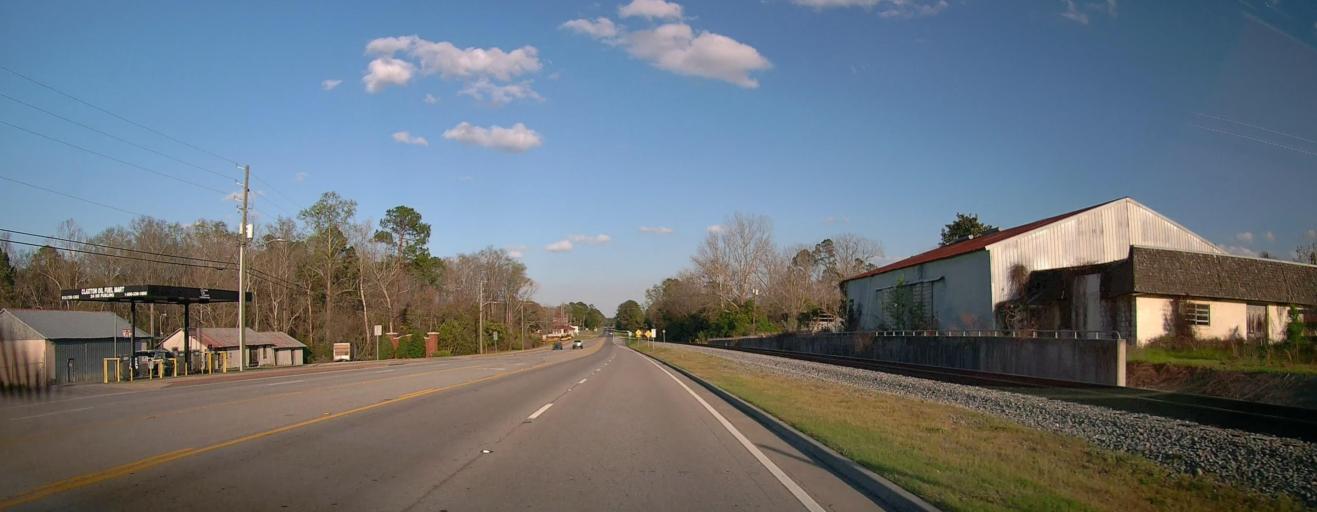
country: US
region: Georgia
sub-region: Evans County
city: Claxton
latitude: 32.1613
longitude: -81.8977
